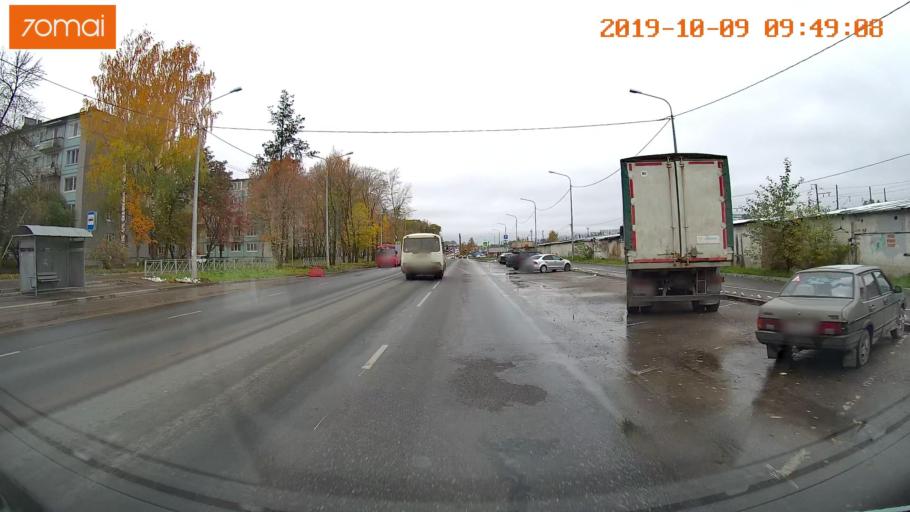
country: RU
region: Vologda
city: Vologda
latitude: 59.1974
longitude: 39.9171
